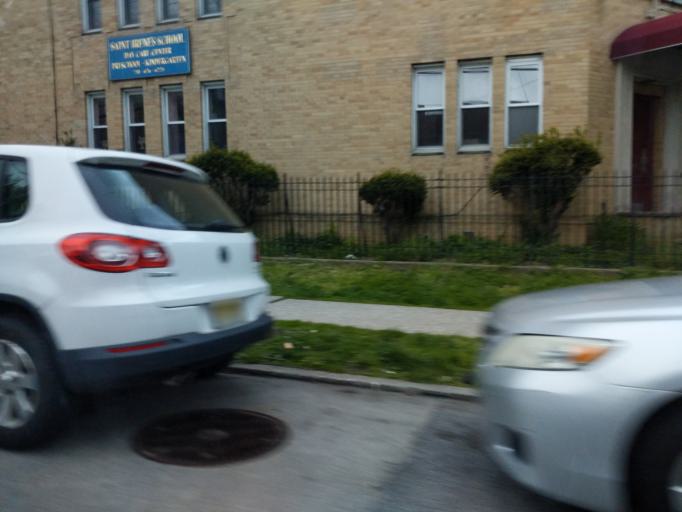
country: US
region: New York
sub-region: Queens County
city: Long Island City
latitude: 40.7715
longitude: -73.9041
